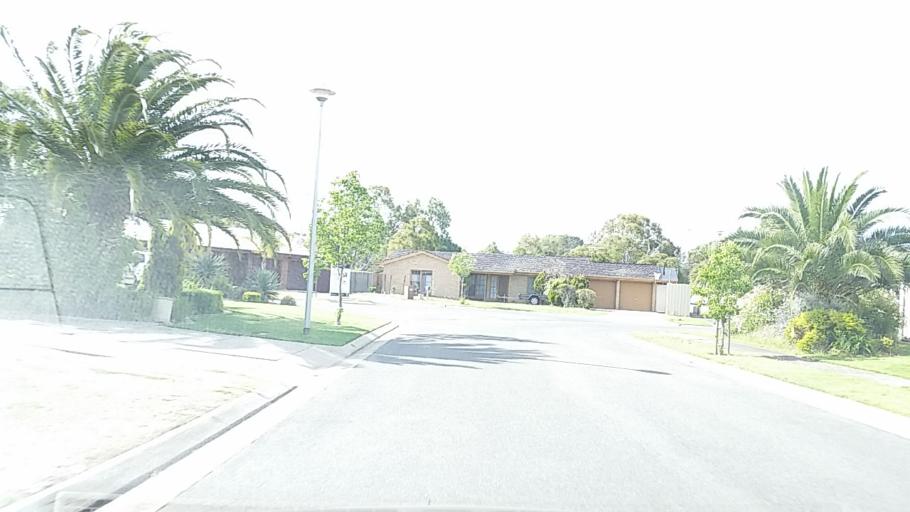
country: AU
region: South Australia
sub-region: Charles Sturt
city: Grange
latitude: -34.8933
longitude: 138.4974
